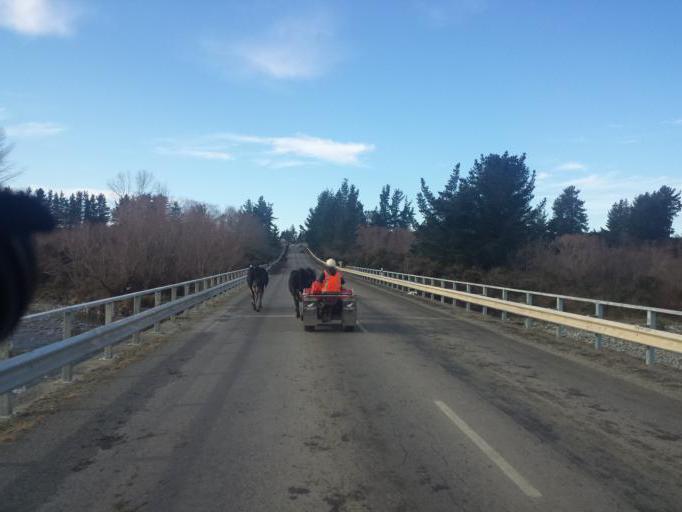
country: NZ
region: Canterbury
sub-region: Timaru District
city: Pleasant Point
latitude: -43.9736
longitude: 171.3028
